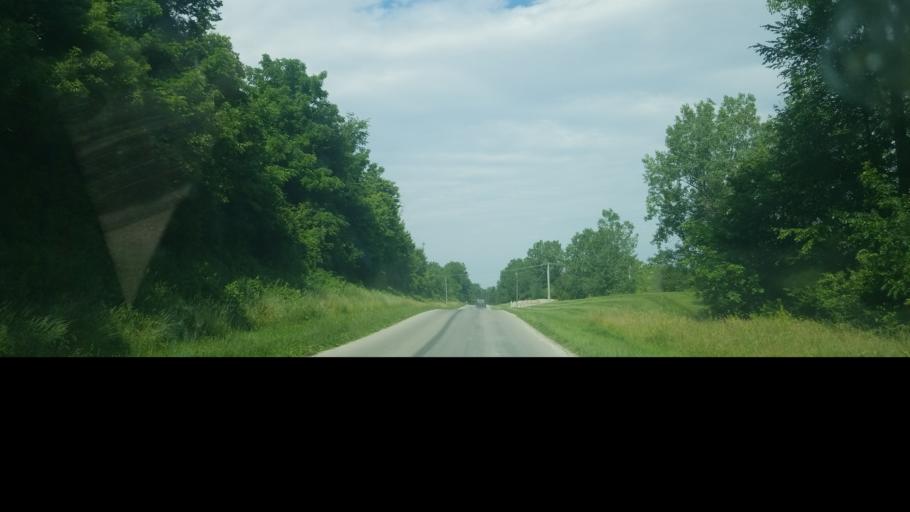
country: US
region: Ohio
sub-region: Wyandot County
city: Carey
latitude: 40.9636
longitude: -83.3718
